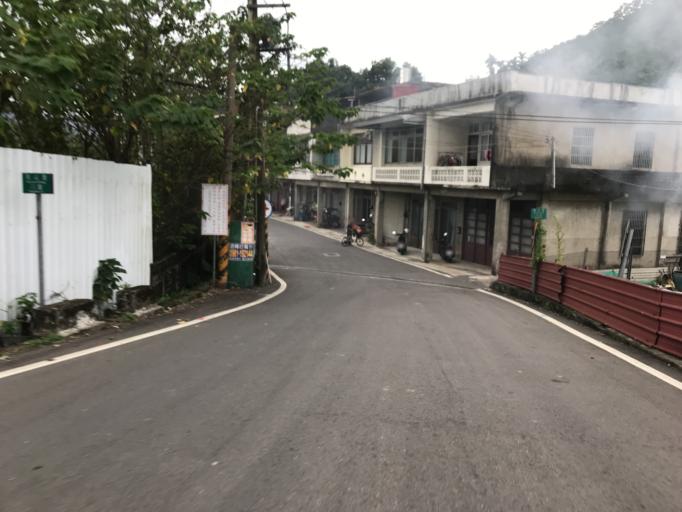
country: TW
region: Taiwan
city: Daxi
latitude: 24.7850
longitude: 121.1753
